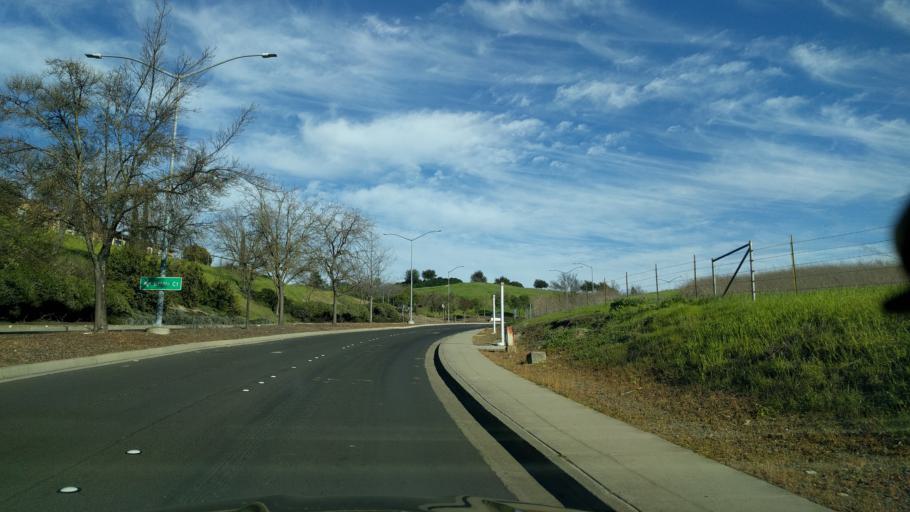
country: US
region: California
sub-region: Alameda County
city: Dublin
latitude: 37.7380
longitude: -121.9236
